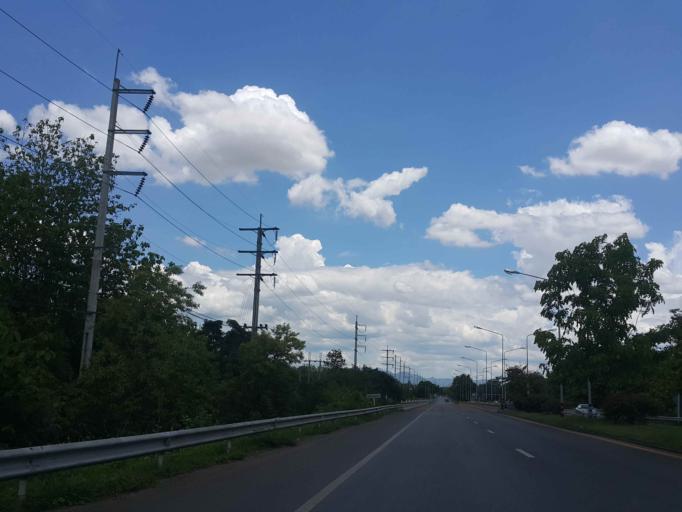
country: TH
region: Phrae
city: Nong Muang Khai
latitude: 18.2190
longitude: 100.1979
